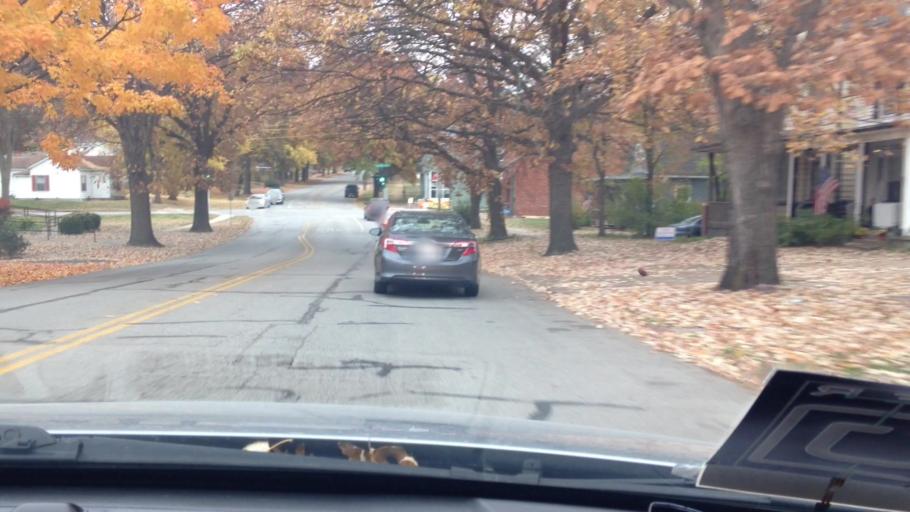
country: US
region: Kansas
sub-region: Leavenworth County
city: Leavenworth
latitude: 39.3112
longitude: -94.9208
